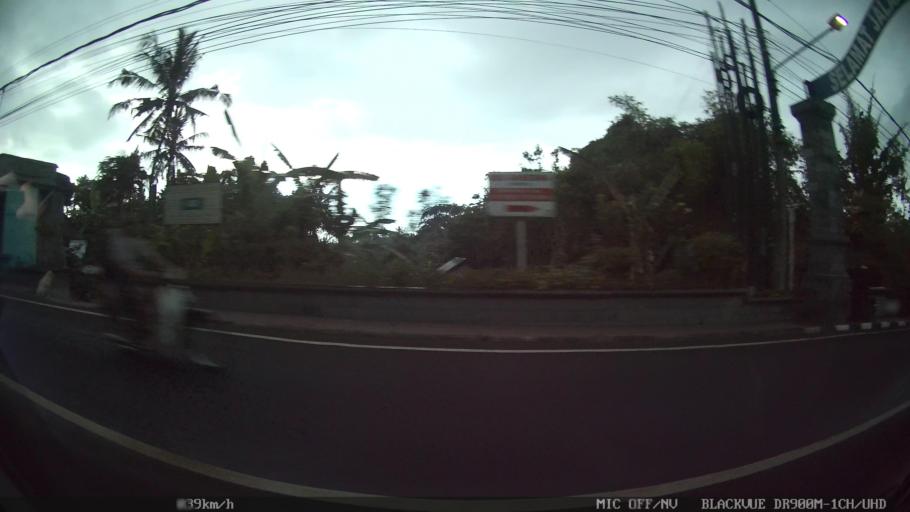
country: ID
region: Bali
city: Banjar Pasekan
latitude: -8.6027
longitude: 115.2823
